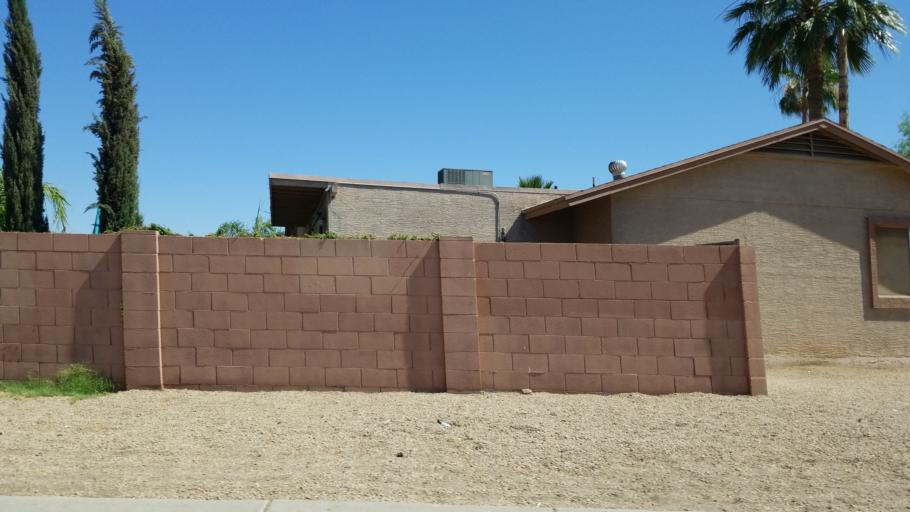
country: US
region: Arizona
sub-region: Maricopa County
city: Tolleson
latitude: 33.4944
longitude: -112.2415
